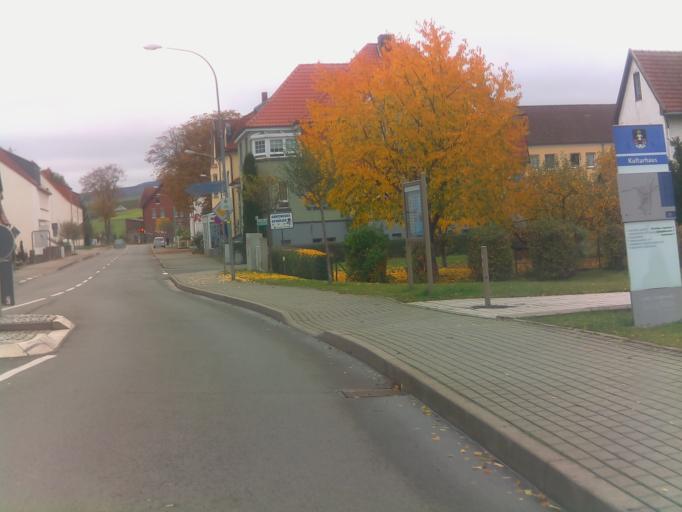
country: DE
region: Thuringia
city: Geisa
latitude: 50.7169
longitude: 9.9535
